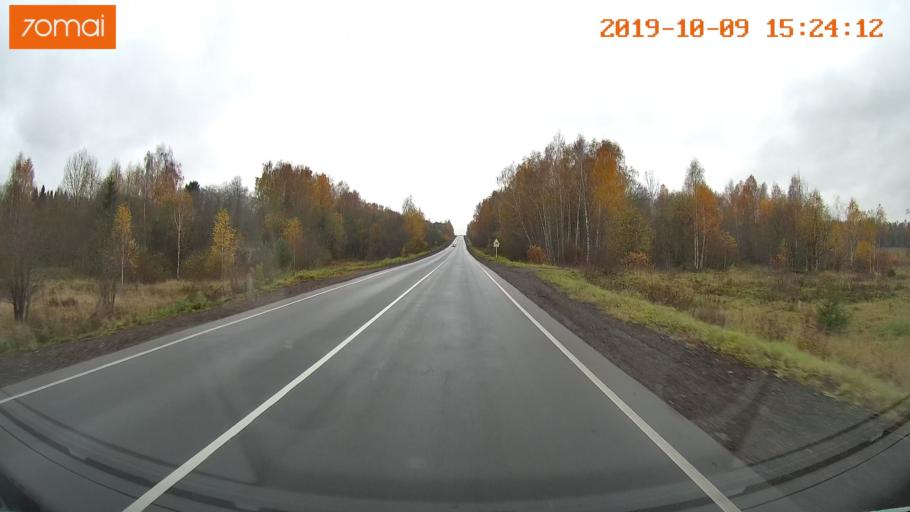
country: RU
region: Kostroma
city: Susanino
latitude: 58.0324
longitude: 41.4592
